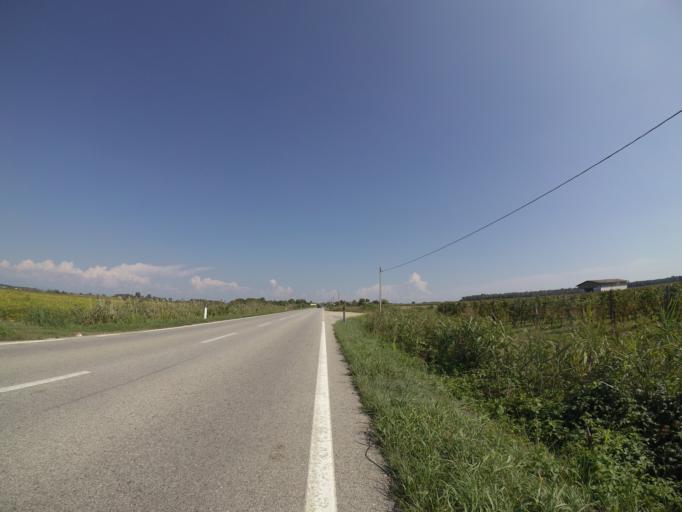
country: IT
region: Friuli Venezia Giulia
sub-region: Provincia di Udine
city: Muzzana del Turgnano
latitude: 45.8146
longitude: 13.1464
